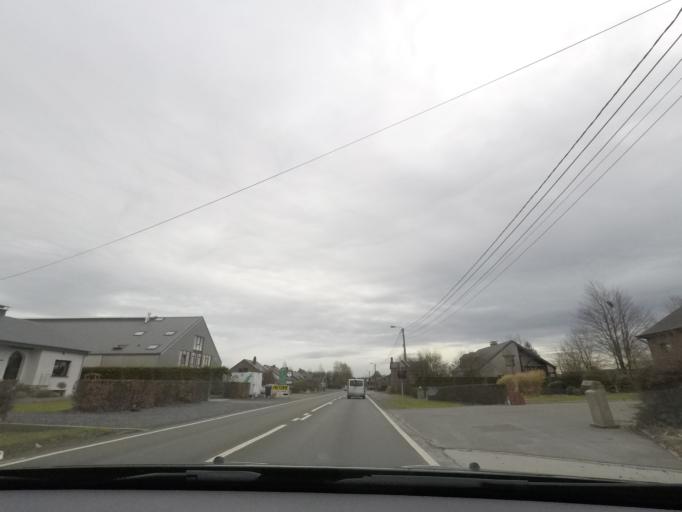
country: BE
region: Wallonia
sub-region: Province du Luxembourg
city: Bastogne
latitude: 49.9907
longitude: 5.7486
